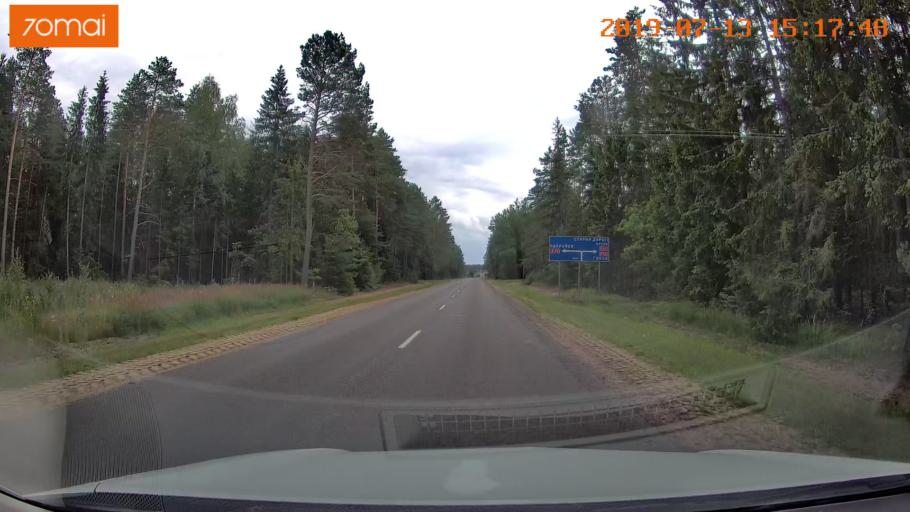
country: BY
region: Mogilev
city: Hlusha
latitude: 53.0914
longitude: 28.8458
